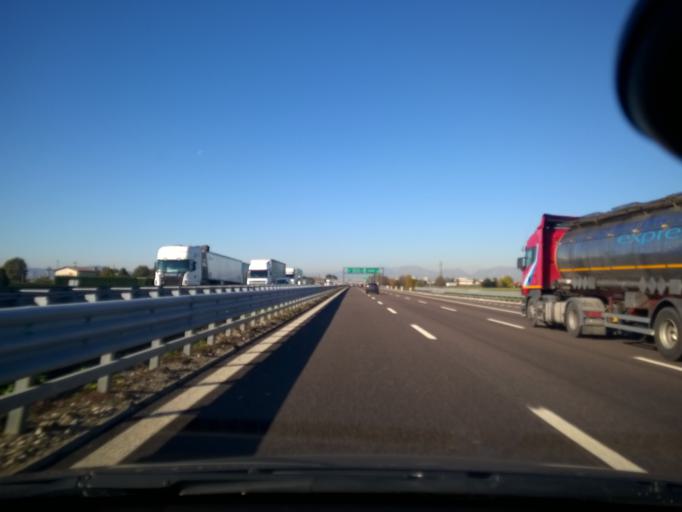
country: IT
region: Veneto
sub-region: Provincia di Vicenza
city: Grisignano di Zocco
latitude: 45.4765
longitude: 11.7126
